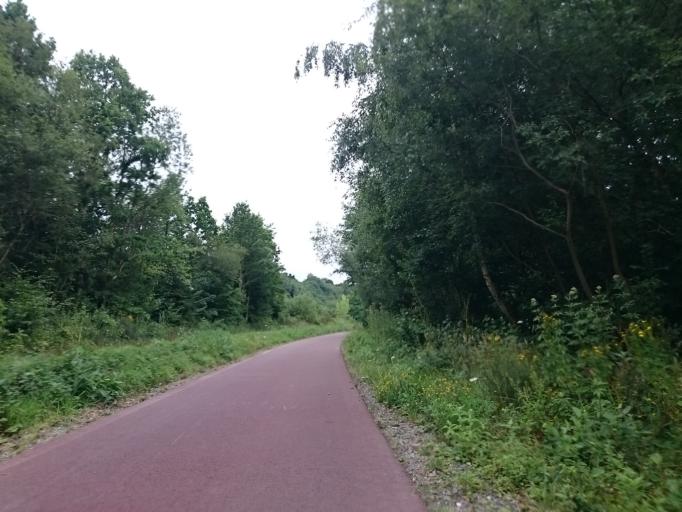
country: FR
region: Lower Normandy
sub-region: Departement du Calvados
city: May-sur-Orne
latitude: 49.1032
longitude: -0.3856
